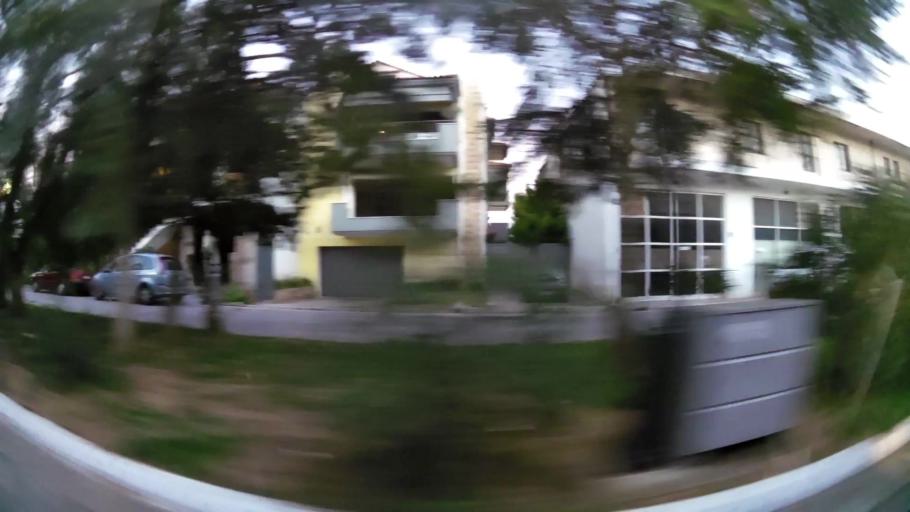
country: GR
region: Attica
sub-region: Nomarchia Anatolikis Attikis
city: Paiania
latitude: 37.9486
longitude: 23.8578
